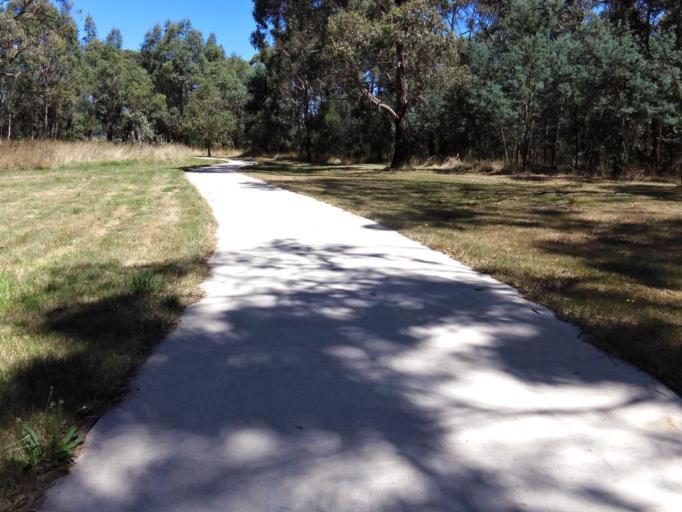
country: AU
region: Victoria
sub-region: Hume
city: Sunbury
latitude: -37.3558
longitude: 144.5403
